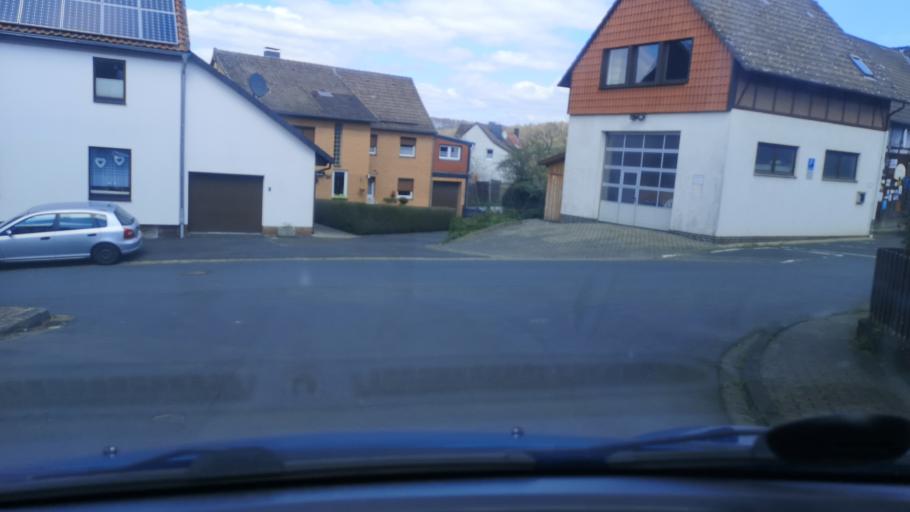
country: DE
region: Lower Saxony
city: Adelebsen
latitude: 51.6490
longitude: 9.7565
